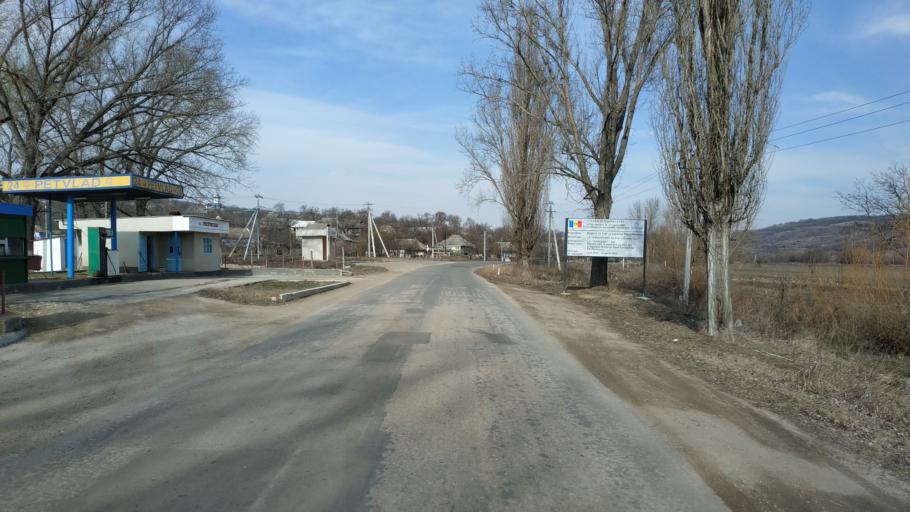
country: MD
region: Nisporeni
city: Nisporeni
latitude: 47.1486
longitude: 28.1083
